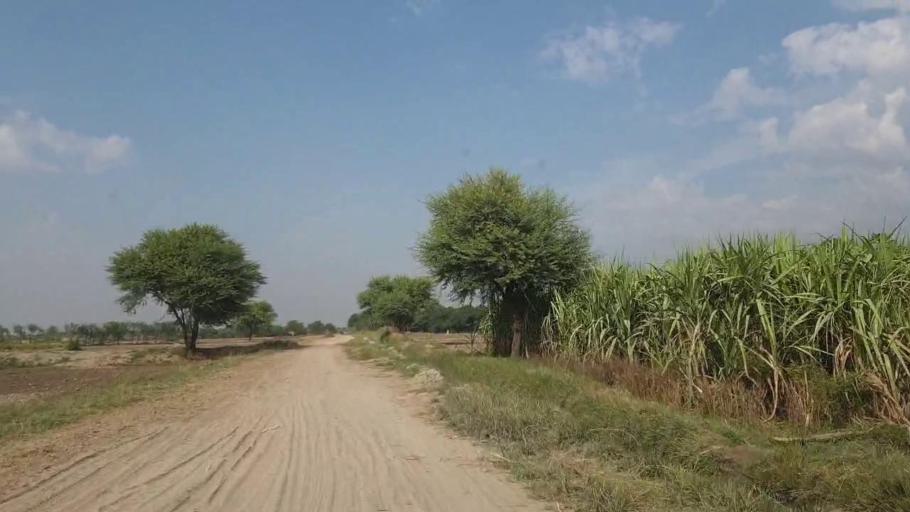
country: PK
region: Sindh
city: Digri
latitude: 25.0281
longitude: 69.0711
